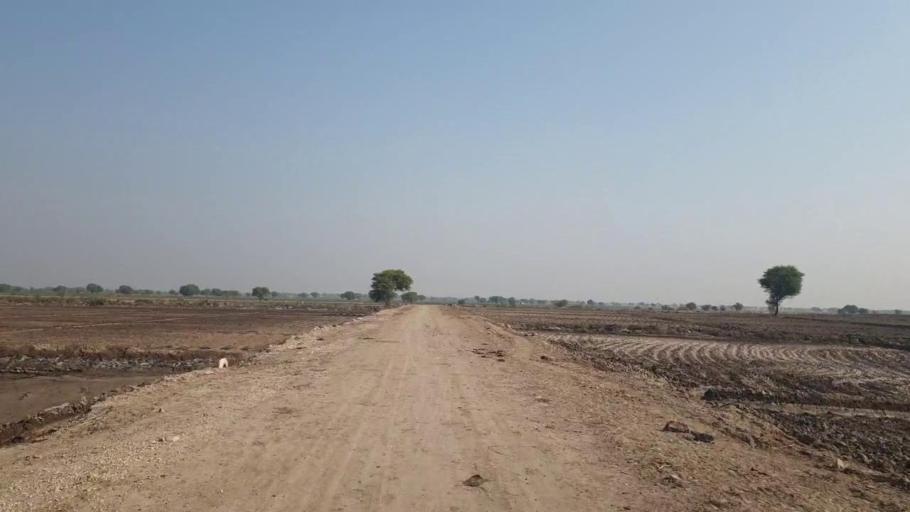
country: PK
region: Sindh
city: Sehwan
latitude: 26.4512
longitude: 67.8293
